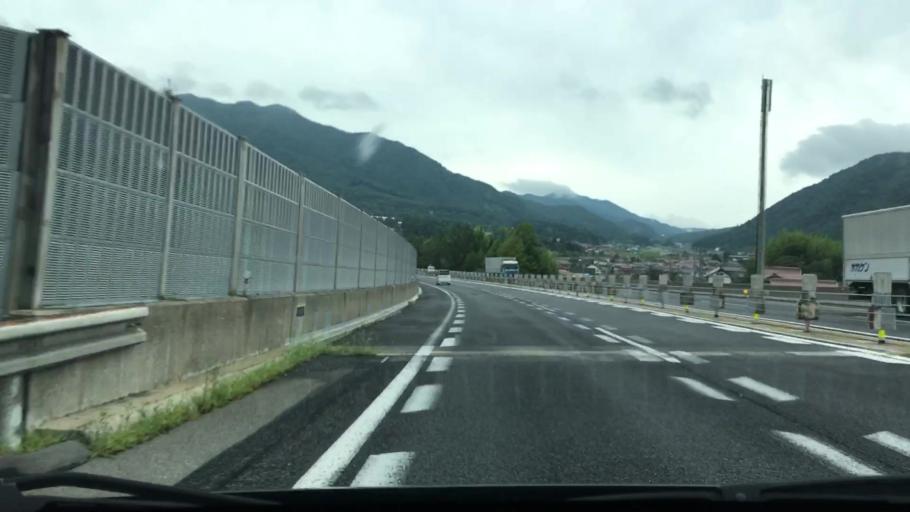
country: JP
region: Hiroshima
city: Hiroshima-shi
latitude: 34.6497
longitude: 132.5169
